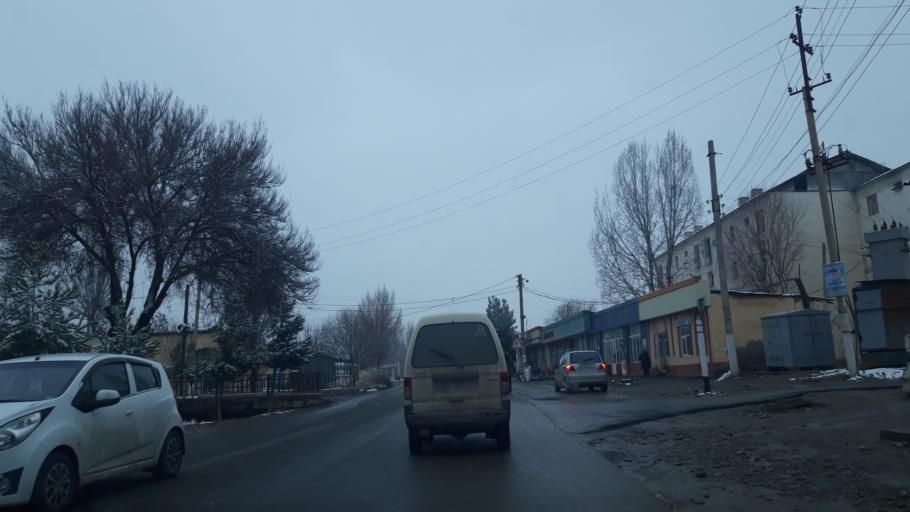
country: UZ
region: Andijon
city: Asaka
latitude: 40.6643
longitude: 72.2399
